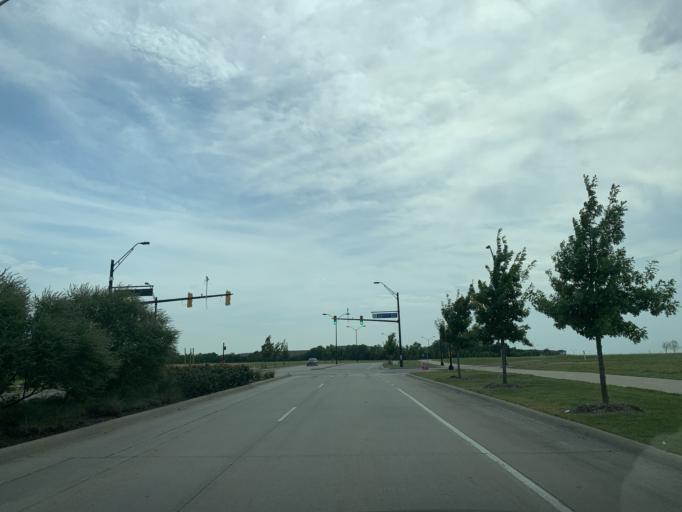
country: US
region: Texas
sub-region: Tarrant County
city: Watauga
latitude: 32.8356
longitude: -97.2816
